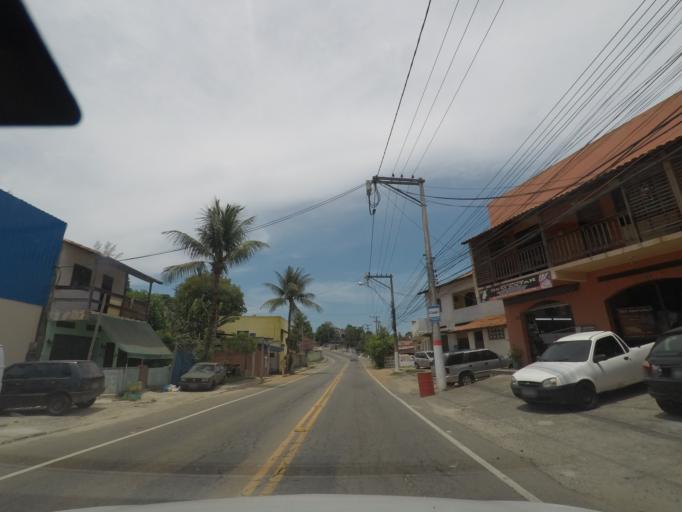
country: BR
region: Rio de Janeiro
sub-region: Marica
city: Marica
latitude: -22.9256
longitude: -42.8194
